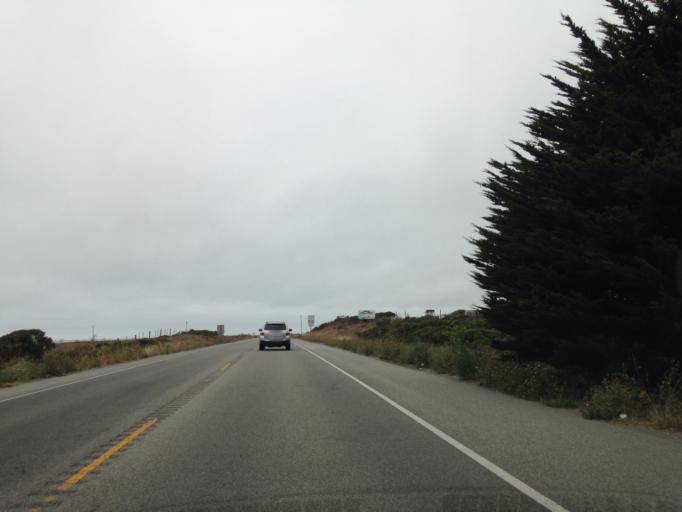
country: US
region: California
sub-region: San Mateo County
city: Half Moon Bay
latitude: 37.3938
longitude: -122.4122
